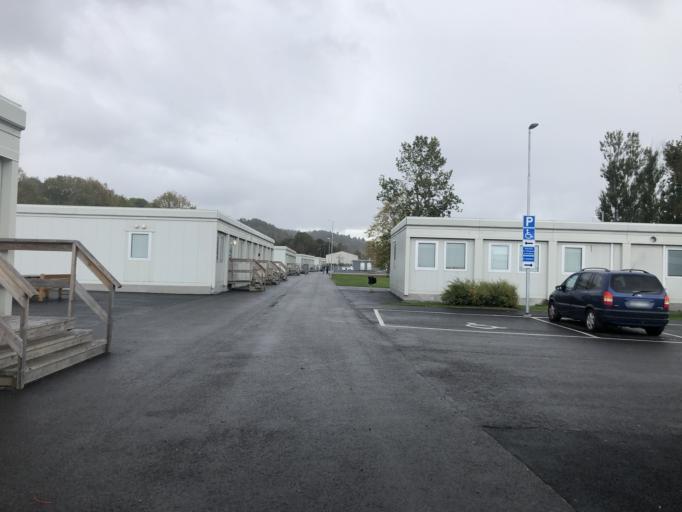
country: SE
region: Vaestra Goetaland
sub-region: Molndal
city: Moelndal
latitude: 57.6517
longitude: 12.0256
